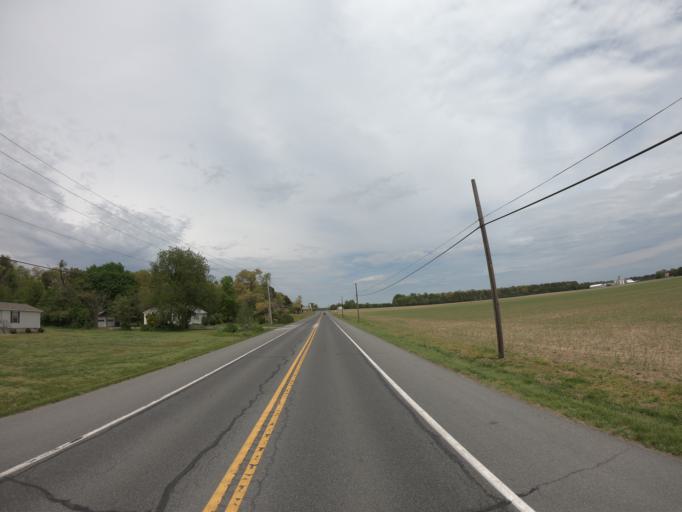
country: US
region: Delaware
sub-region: Sussex County
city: Milton
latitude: 38.7996
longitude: -75.2808
